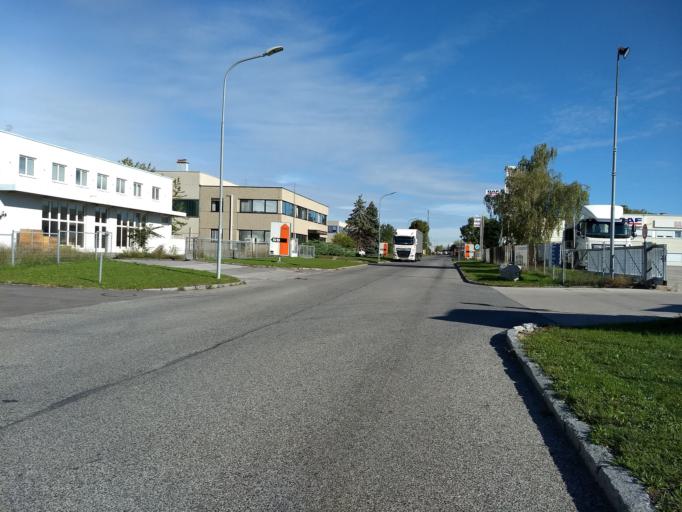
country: AT
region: Lower Austria
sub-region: Politischer Bezirk Modling
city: Neu-Guntramsdorf
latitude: 48.0637
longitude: 16.3289
